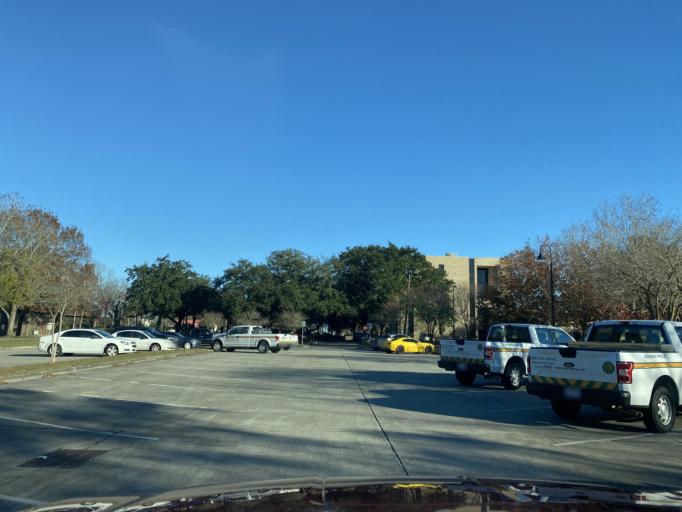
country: US
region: Louisiana
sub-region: Jefferson Parish
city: Kenner
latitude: 29.9908
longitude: -90.2437
